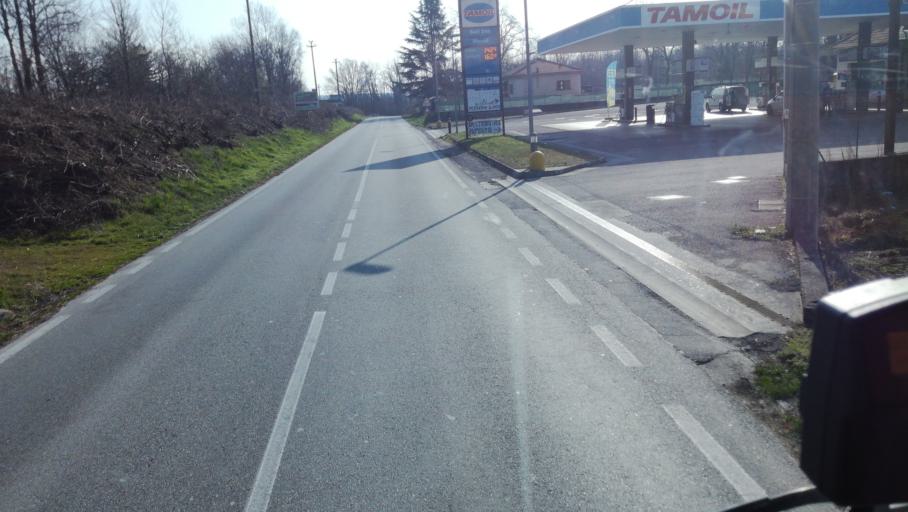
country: IT
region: Piedmont
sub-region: Provincia di Novara
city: Oleggio
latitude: 45.5916
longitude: 8.6715
